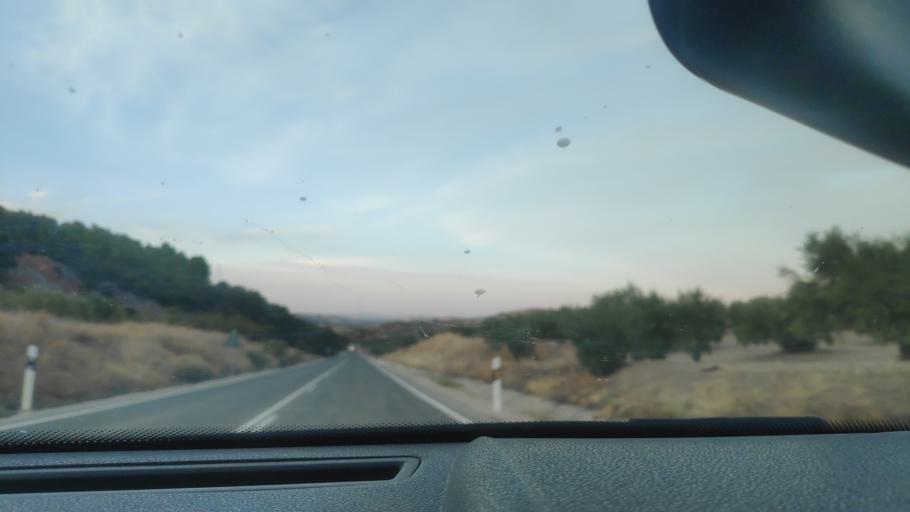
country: ES
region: Andalusia
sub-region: Provincia de Jaen
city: Villardompardo
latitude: 37.8323
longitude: -4.0486
